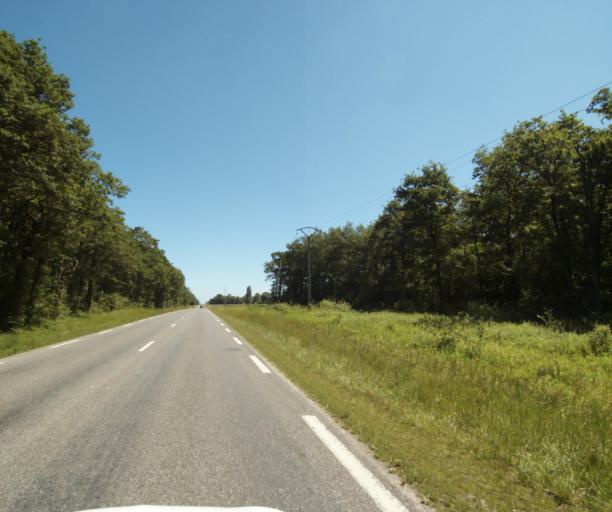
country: FR
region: Rhone-Alpes
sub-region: Departement de la Haute-Savoie
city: Veigy-Foncenex
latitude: 46.2874
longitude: 6.2669
